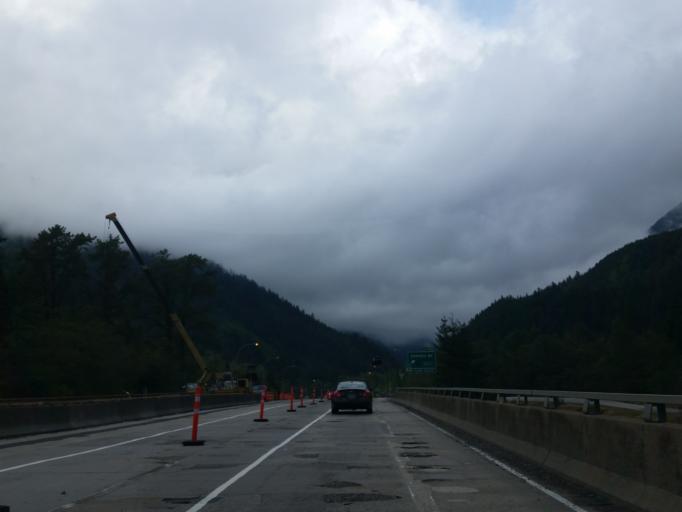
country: CA
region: British Columbia
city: Hope
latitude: 49.3850
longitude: -121.3186
